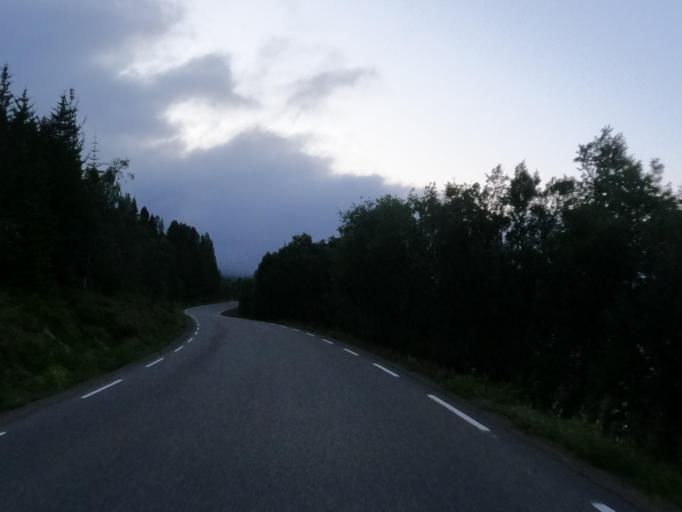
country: NO
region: Nordland
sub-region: Lodingen
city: Lodingen
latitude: 68.5985
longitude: 15.7889
